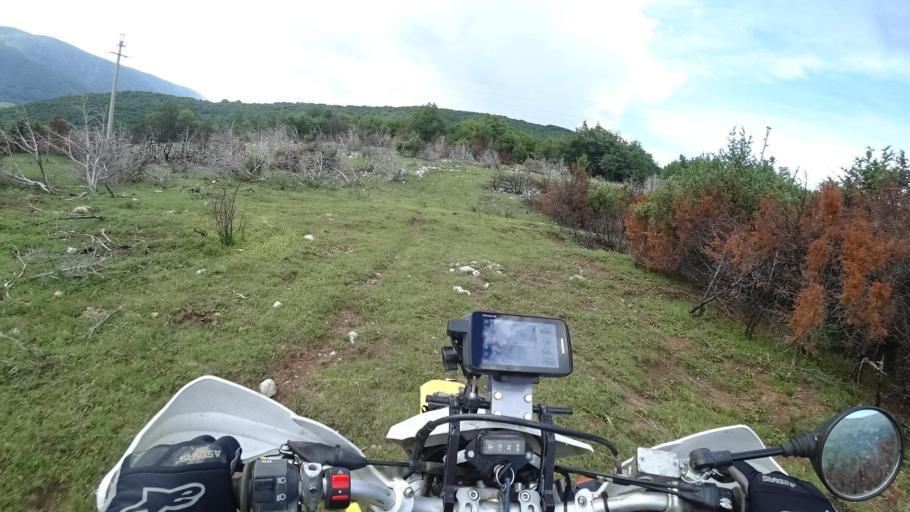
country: BA
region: Federation of Bosnia and Herzegovina
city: Izacic
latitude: 44.7706
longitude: 15.7193
